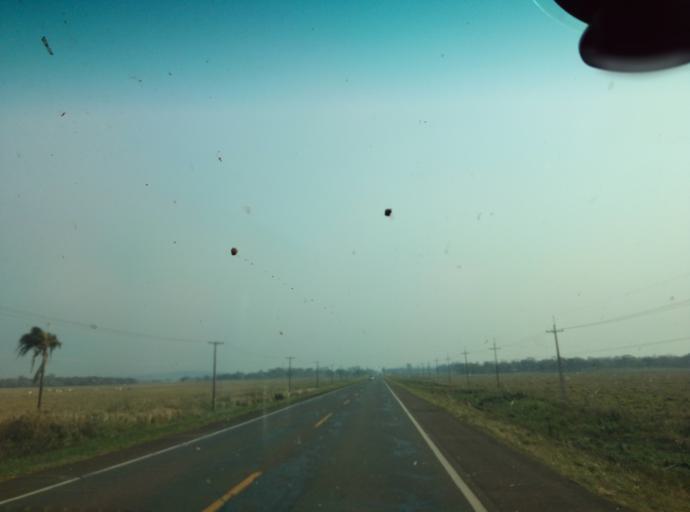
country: PY
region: Caaguazu
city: Carayao
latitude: -25.1304
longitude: -56.3541
